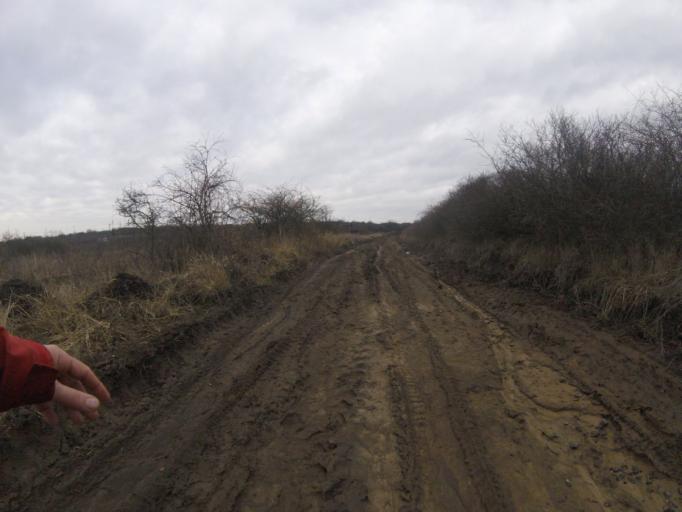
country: HU
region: Heves
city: Egerszalok
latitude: 47.8490
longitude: 20.3416
